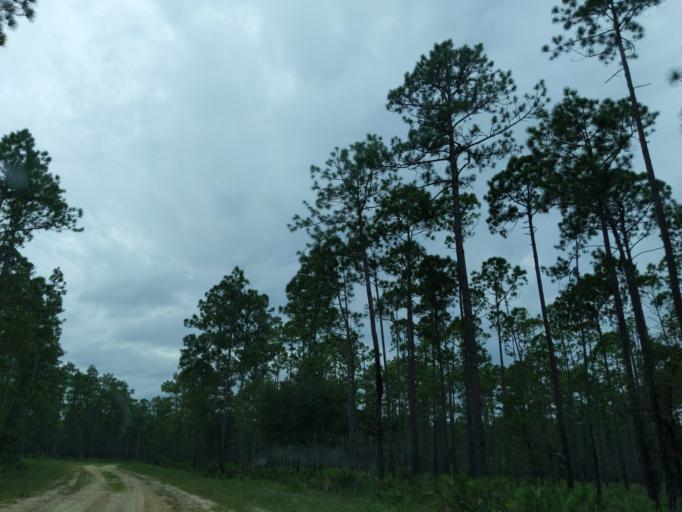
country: US
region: Florida
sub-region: Gadsden County
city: Midway
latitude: 30.3505
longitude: -84.5085
